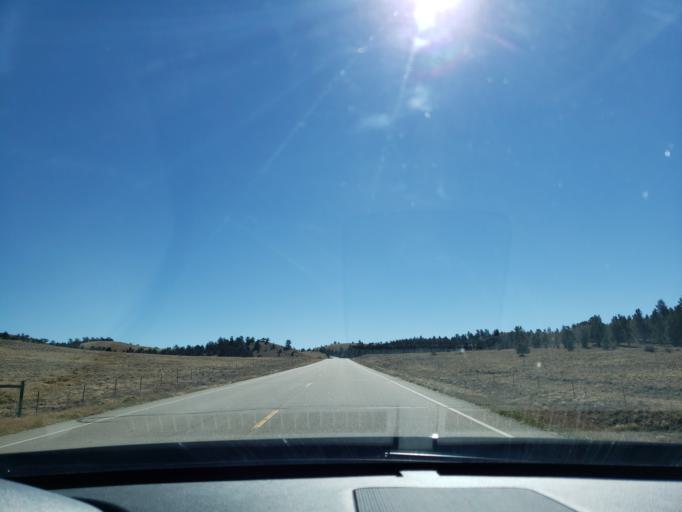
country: US
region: Colorado
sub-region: Chaffee County
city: Buena Vista
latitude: 38.9009
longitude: -105.6946
